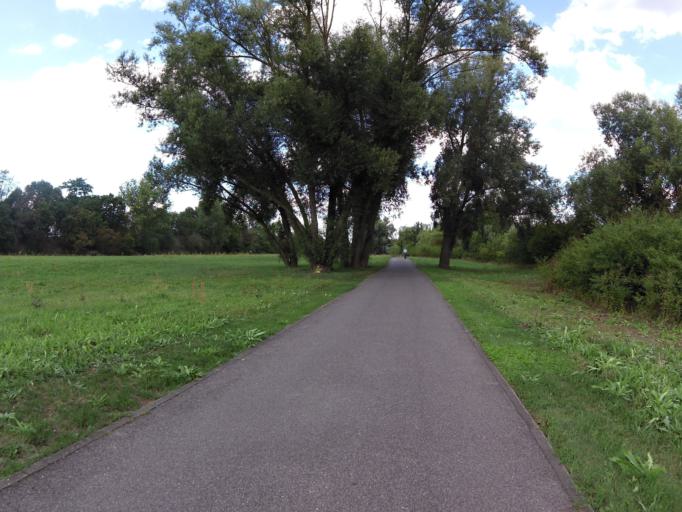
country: DE
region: Bavaria
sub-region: Regierungsbezirk Unterfranken
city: Schweinfurt
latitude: 50.0299
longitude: 10.2188
